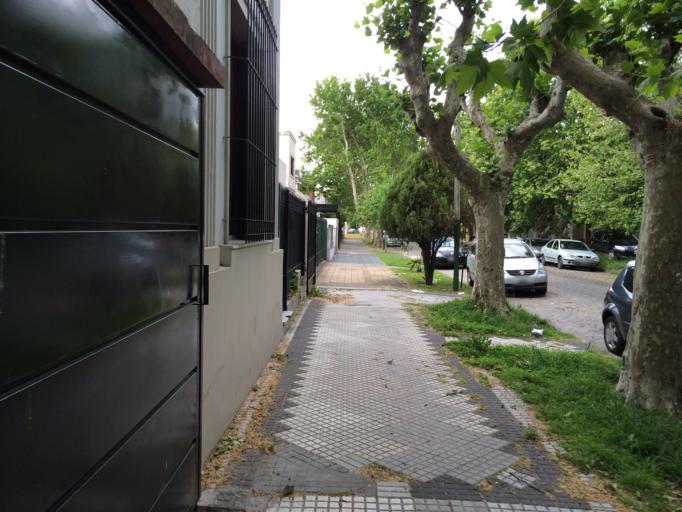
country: AR
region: Buenos Aires
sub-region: Partido de Lomas de Zamora
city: Lomas de Zamora
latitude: -34.7561
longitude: -58.3972
